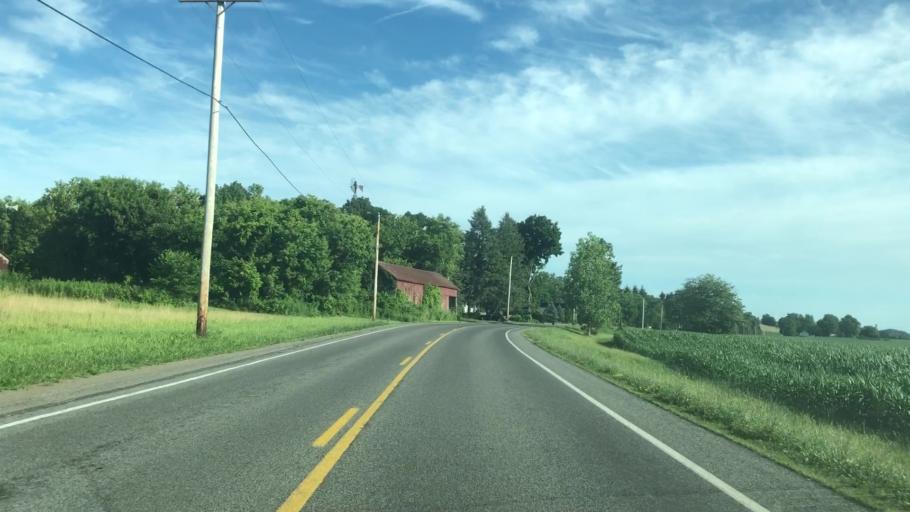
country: US
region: New York
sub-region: Wayne County
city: Macedon
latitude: 43.1149
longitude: -77.3032
